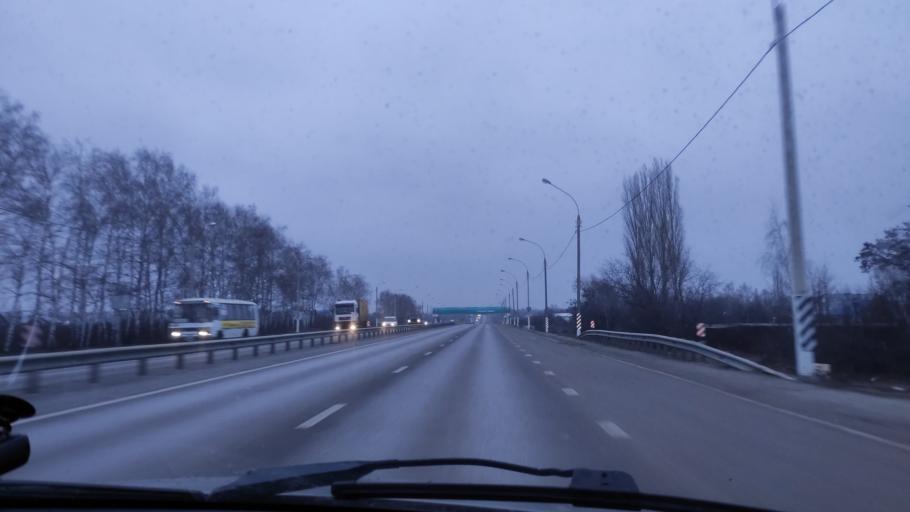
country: RU
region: Tambov
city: Komsomolets
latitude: 52.7305
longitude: 41.3149
